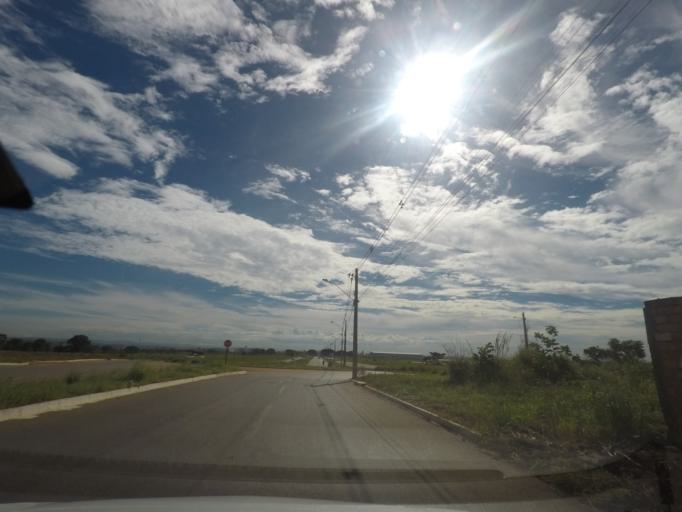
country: BR
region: Goias
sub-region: Aparecida De Goiania
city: Aparecida de Goiania
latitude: -16.8098
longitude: -49.2775
